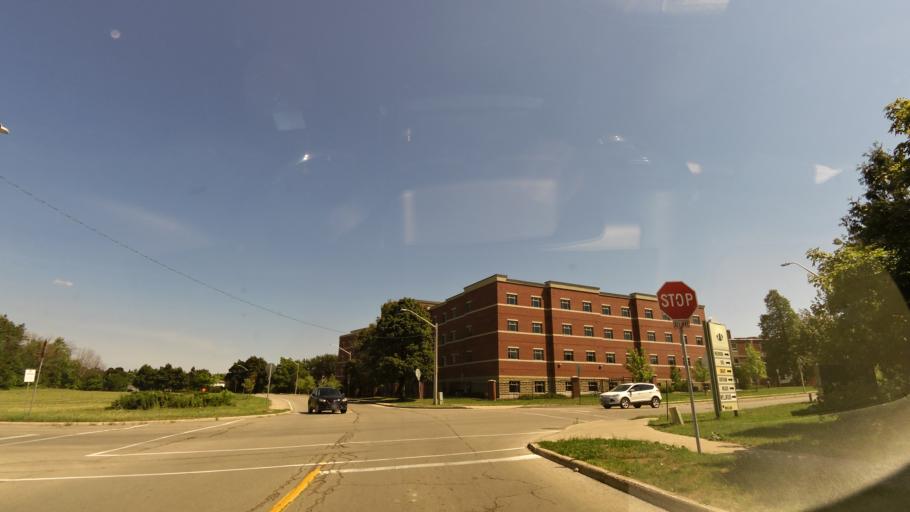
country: CA
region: Ontario
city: Hamilton
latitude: 43.2424
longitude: -79.9154
